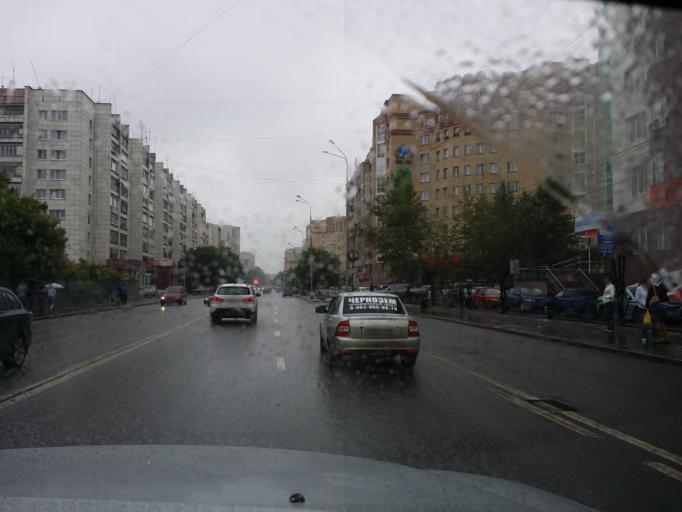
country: RU
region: Tjumen
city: Tyumen
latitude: 57.1453
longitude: 65.5454
